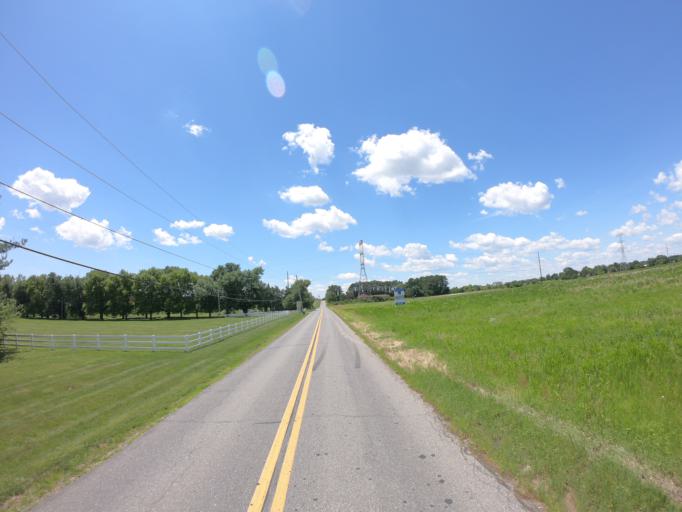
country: US
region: Delaware
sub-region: New Castle County
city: Middletown
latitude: 39.4810
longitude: -75.7708
